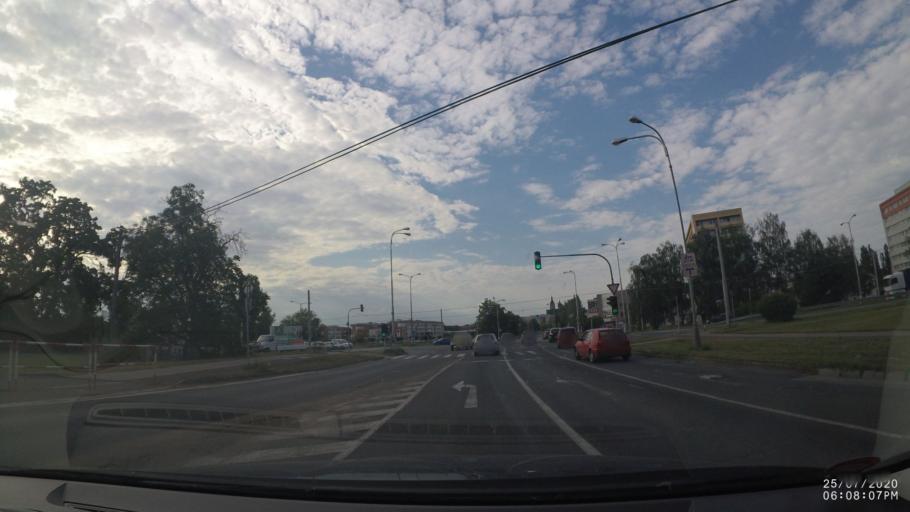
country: CZ
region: Kralovehradecky
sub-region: Okres Hradec Kralove
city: Hradec Kralove
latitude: 50.2007
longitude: 15.8327
